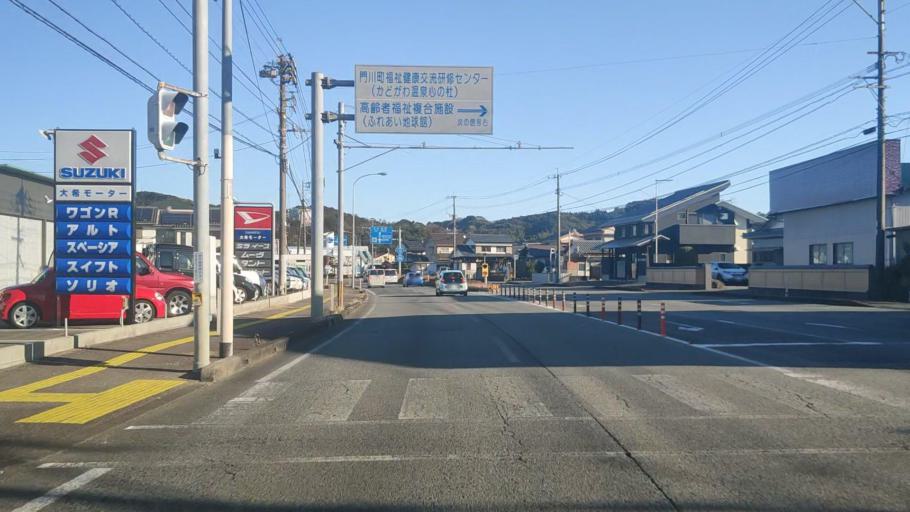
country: JP
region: Miyazaki
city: Nobeoka
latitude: 32.4866
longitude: 131.6636
